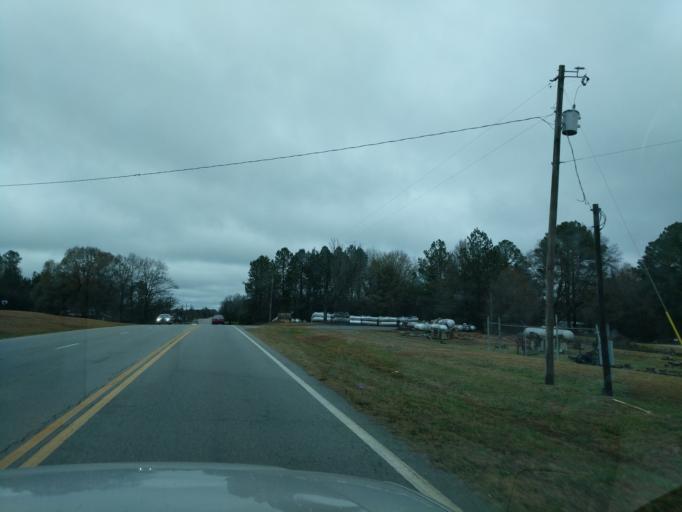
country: US
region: Georgia
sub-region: Hart County
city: Royston
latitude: 34.3187
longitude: -83.1108
